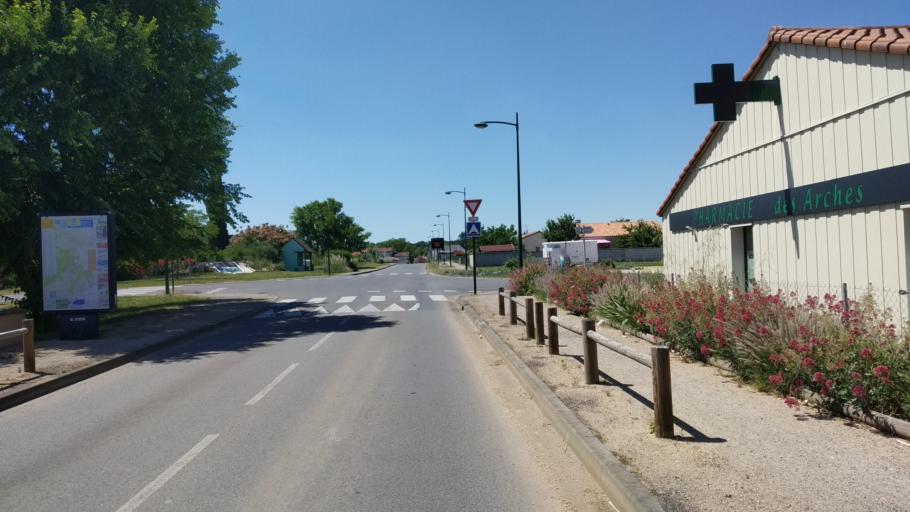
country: FR
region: Poitou-Charentes
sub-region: Departement de la Vienne
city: Vouneuil-sous-Biard
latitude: 46.6052
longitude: 0.2769
